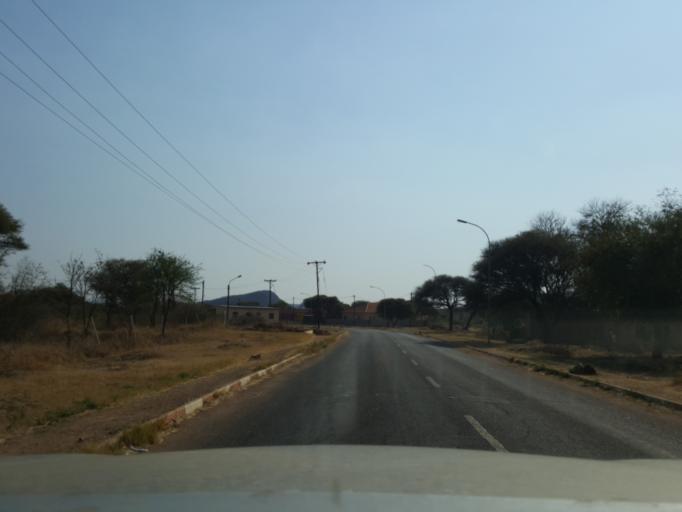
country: BW
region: South East
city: Lobatse
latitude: -25.1943
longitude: 25.6942
